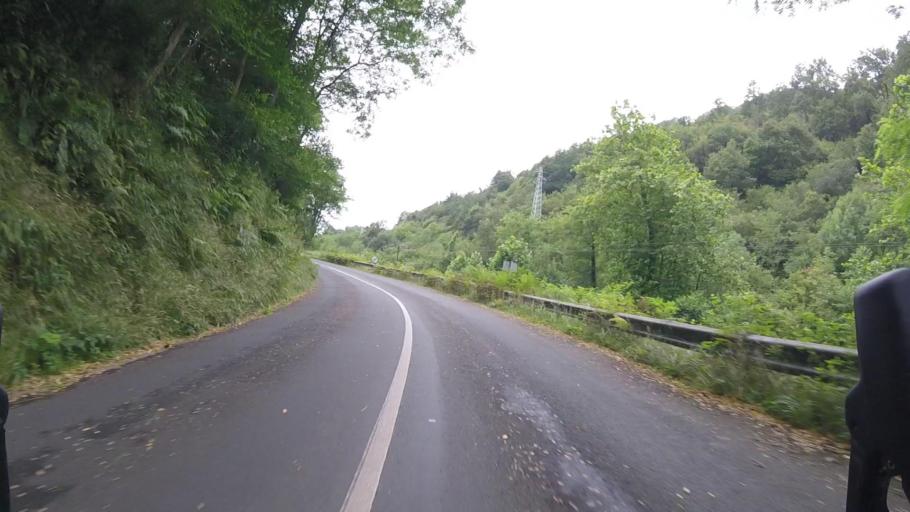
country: ES
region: Basque Country
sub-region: Provincia de Guipuzcoa
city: Irun
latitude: 43.2847
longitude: -1.8233
